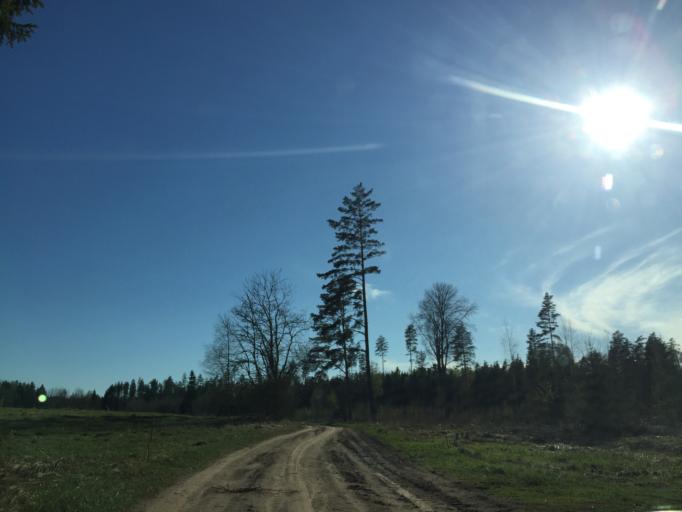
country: EE
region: Valgamaa
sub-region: Valga linn
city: Valga
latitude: 57.7812
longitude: 26.2359
